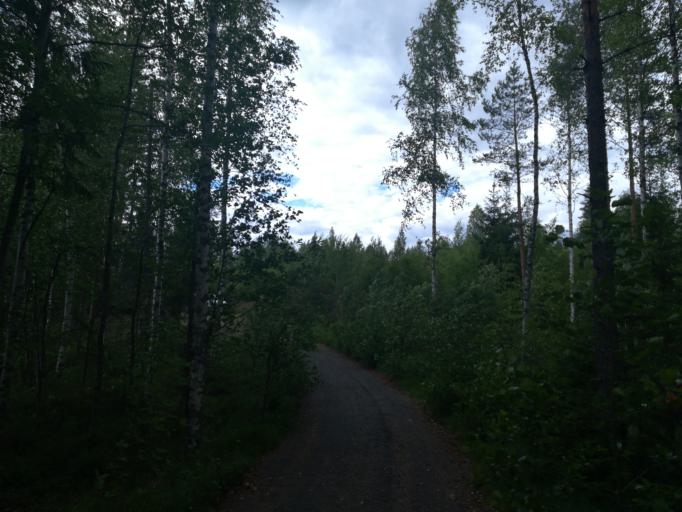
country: FI
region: Southern Savonia
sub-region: Mikkeli
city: Mikkeli
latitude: 61.6717
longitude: 27.1114
